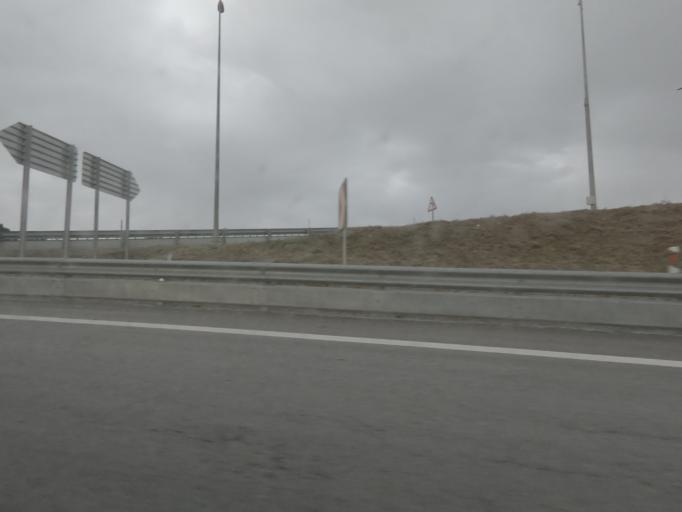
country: PT
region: Vila Real
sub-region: Vila Real
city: Vila Real
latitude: 41.2945
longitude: -7.6902
